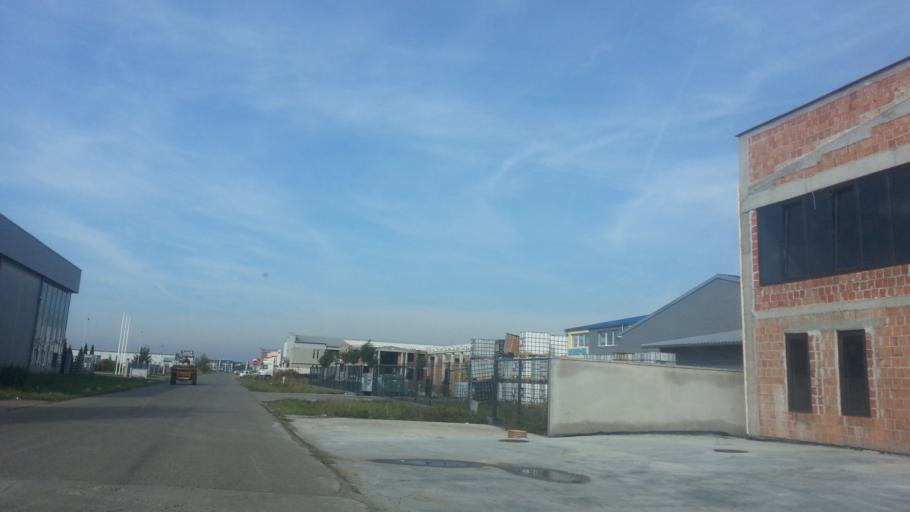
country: RS
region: Autonomna Pokrajina Vojvodina
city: Nova Pazova
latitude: 44.9507
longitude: 20.1993
